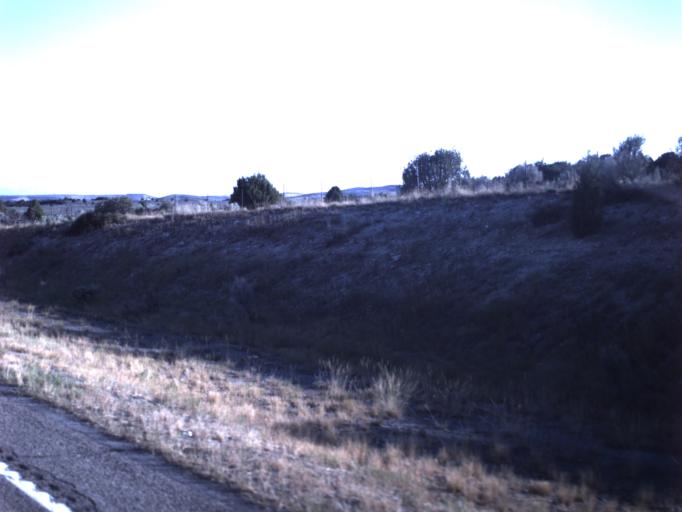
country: US
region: Utah
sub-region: Sanpete County
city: Fairview
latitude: 39.6885
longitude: -111.4596
